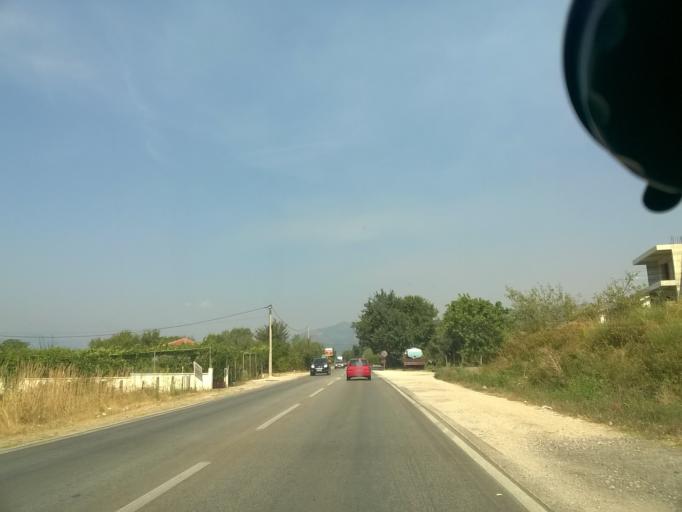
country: ME
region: Kotor
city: Kotor
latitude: 42.3732
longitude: 18.7529
